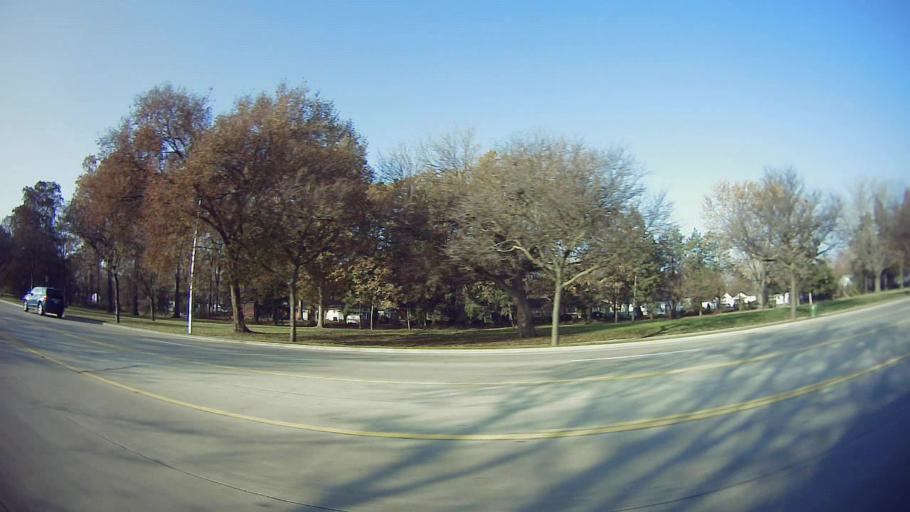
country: US
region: Michigan
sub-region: Oakland County
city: Oak Park
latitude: 42.4523
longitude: -83.1816
